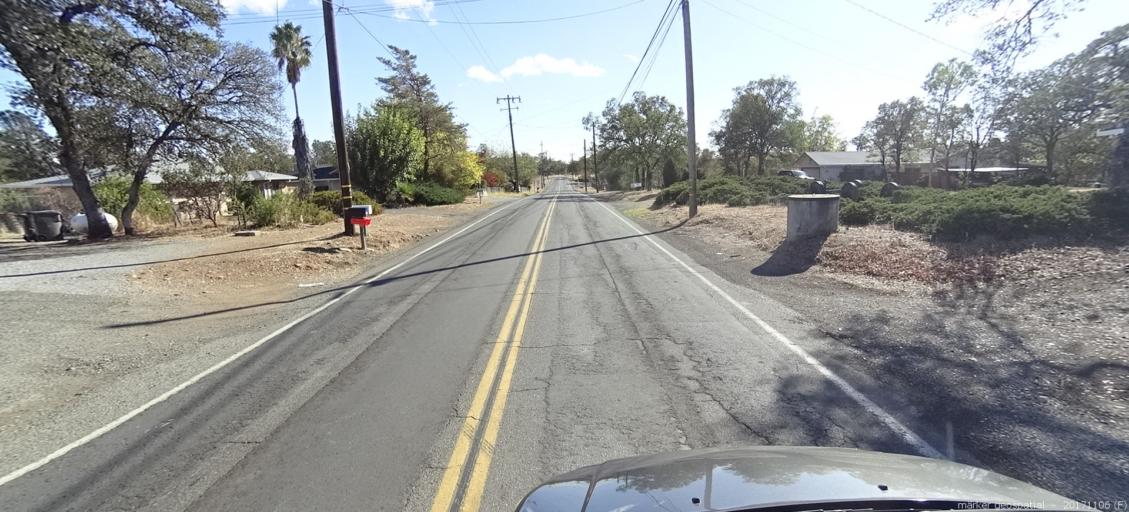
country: US
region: California
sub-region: Shasta County
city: Palo Cedro
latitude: 40.5726
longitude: -122.3015
